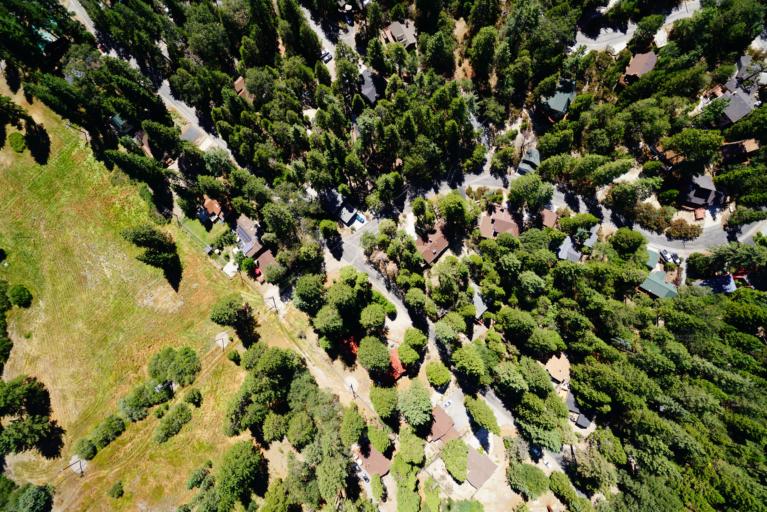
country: US
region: California
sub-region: Riverside County
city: Idyllwild-Pine Cove
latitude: 33.7556
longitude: -116.7323
